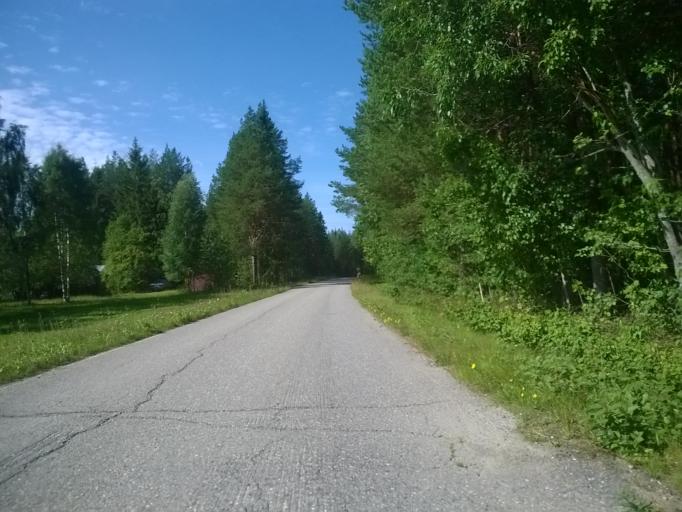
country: FI
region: Kainuu
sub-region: Kehys-Kainuu
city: Kuhmo
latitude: 64.1288
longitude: 29.3889
